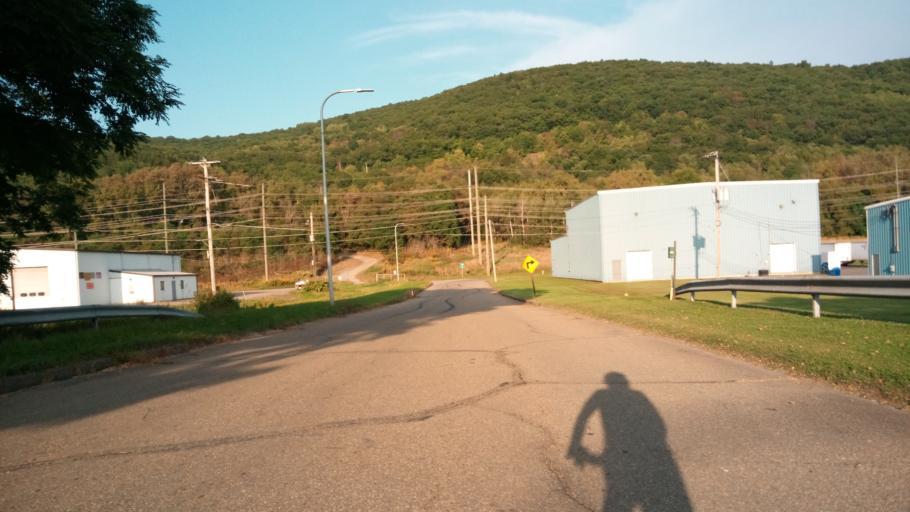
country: US
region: New York
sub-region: Chemung County
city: Elmira
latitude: 42.1126
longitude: -76.8011
